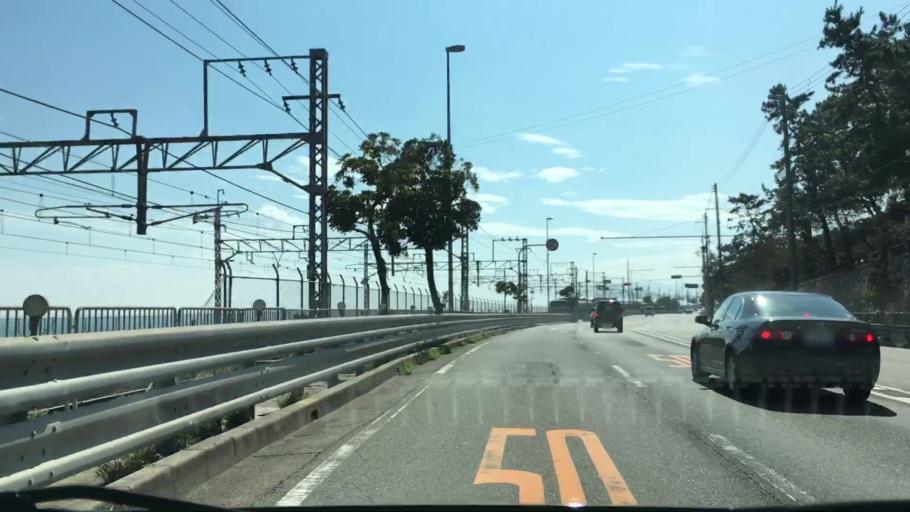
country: JP
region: Hyogo
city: Kobe
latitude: 34.6376
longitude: 135.1019
